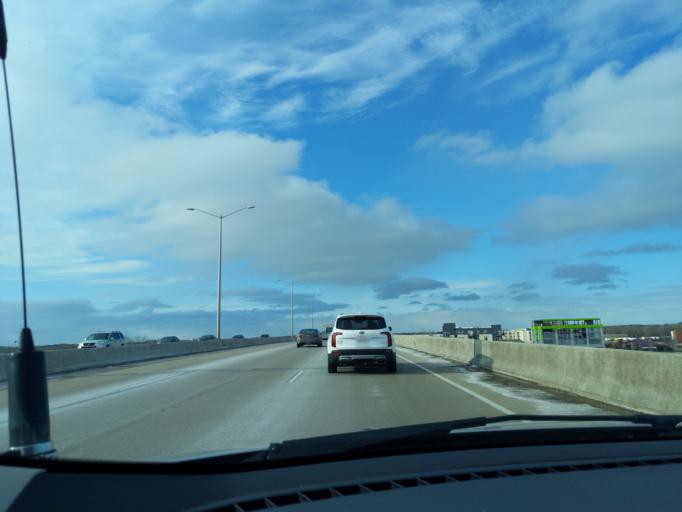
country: US
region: Wisconsin
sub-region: Brown County
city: Ashwaubenon
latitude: 44.4753
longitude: -88.0438
